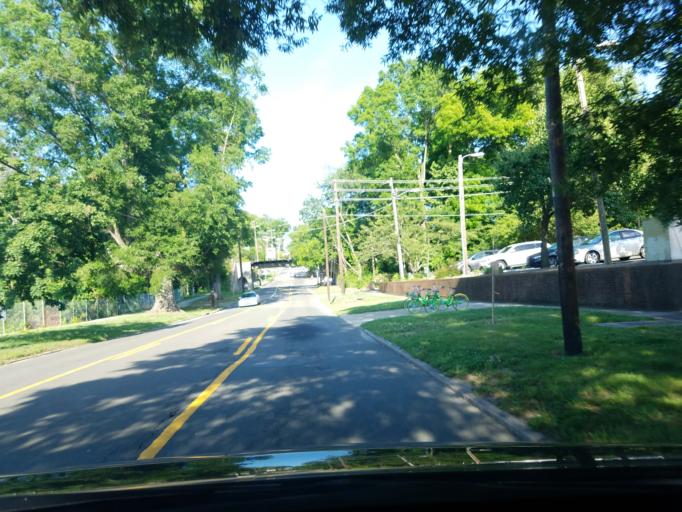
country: US
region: North Carolina
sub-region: Durham County
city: Durham
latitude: 36.0055
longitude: -78.9043
